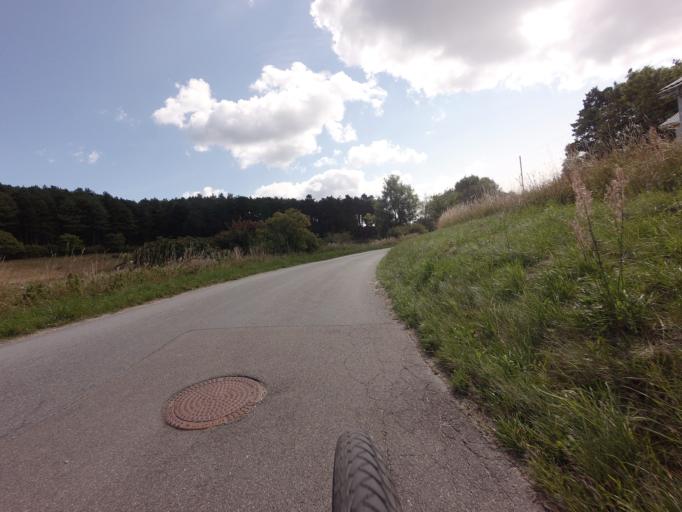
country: DK
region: Zealand
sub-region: Vordingborg Kommune
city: Stege
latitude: 54.9584
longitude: 12.5330
